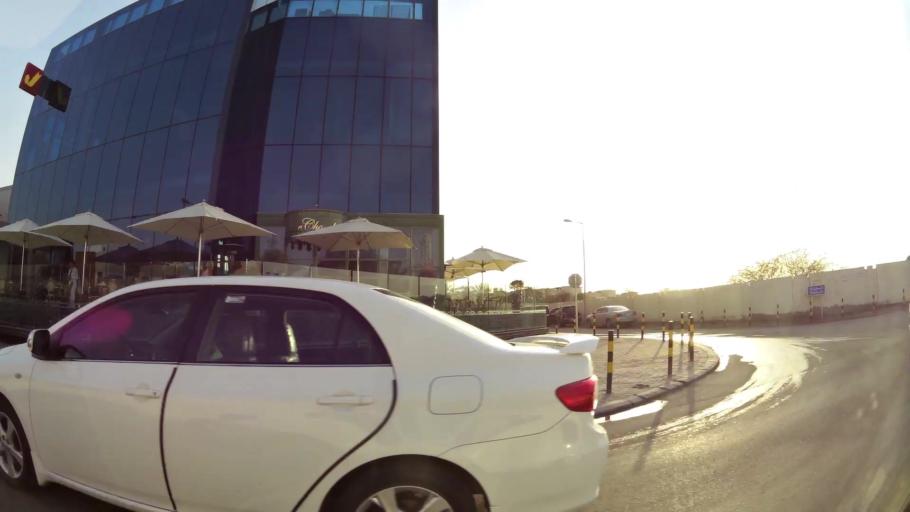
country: BH
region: Manama
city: Jidd Hafs
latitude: 26.2009
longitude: 50.4979
